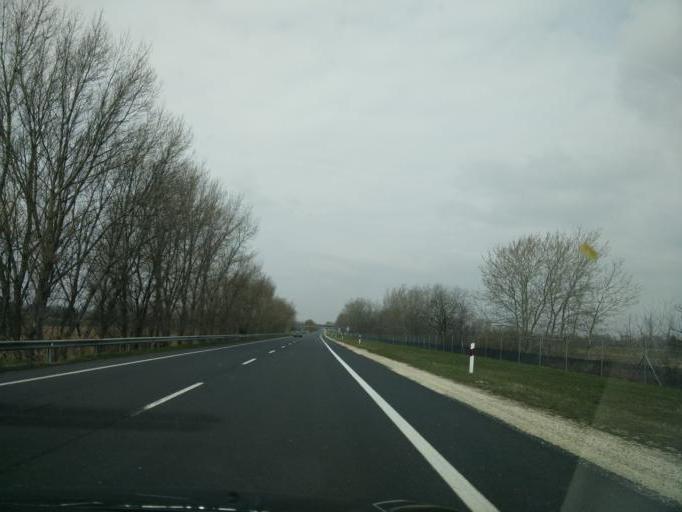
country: HU
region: Gyor-Moson-Sopron
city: Toltestava
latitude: 47.6976
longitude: 17.7767
